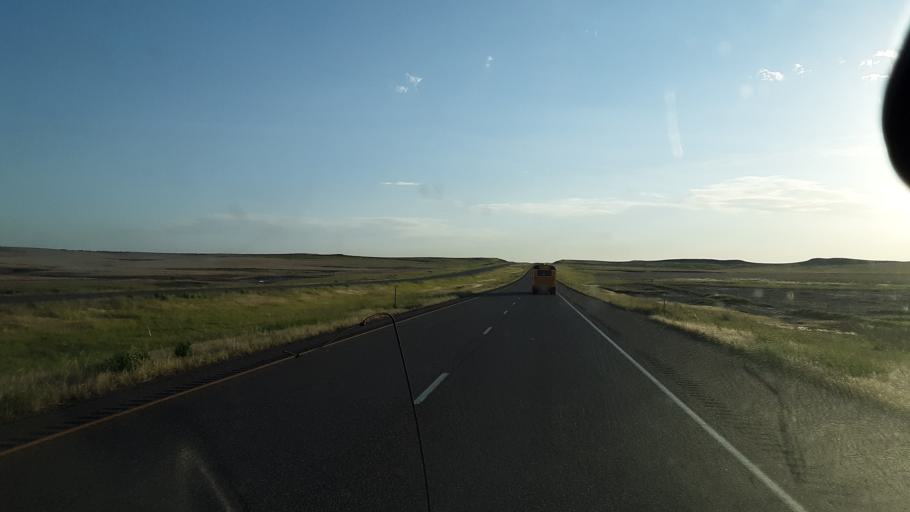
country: US
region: Montana
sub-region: Big Horn County
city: Hardin
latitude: 45.7454
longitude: -107.7006
